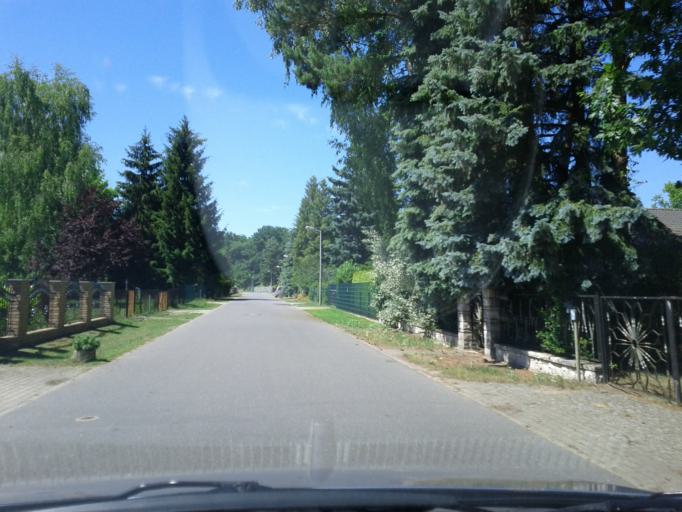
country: DE
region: Brandenburg
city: Spreenhagen
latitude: 52.3944
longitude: 13.9399
